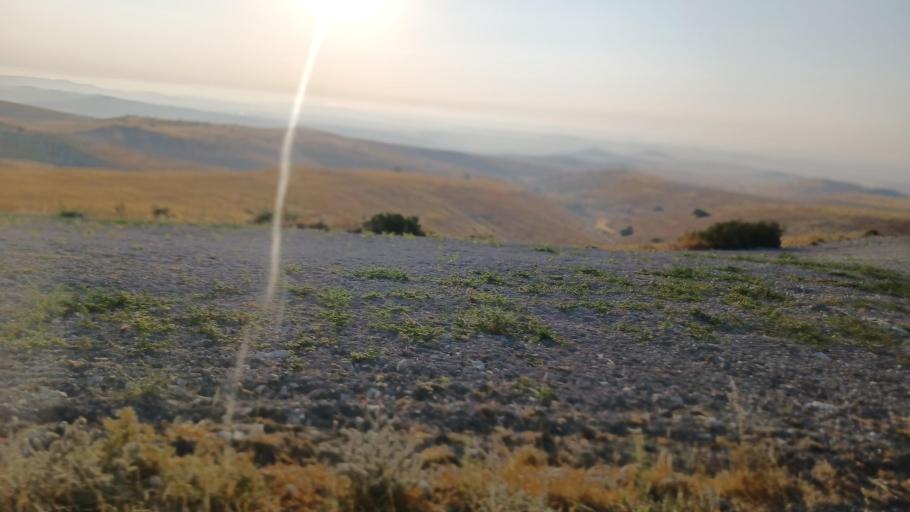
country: CY
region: Larnaka
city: Psevdas
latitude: 34.9142
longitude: 33.4856
